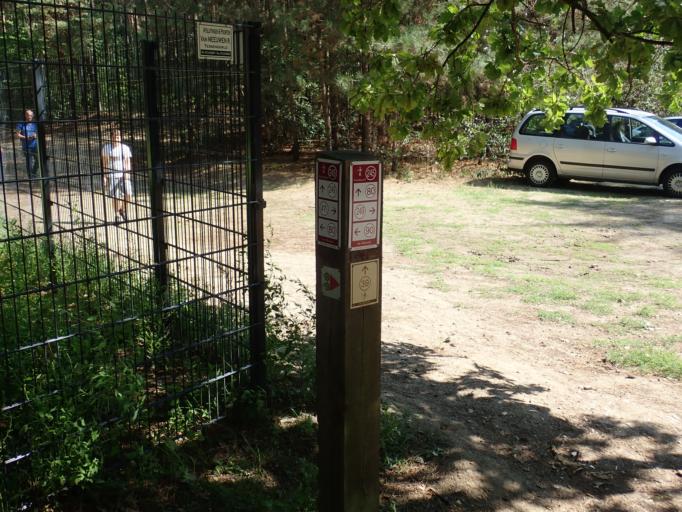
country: BE
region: Flanders
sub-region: Provincie Vlaams-Brabant
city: Scherpenheuvel-Zichem
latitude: 51.0259
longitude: 4.9966
